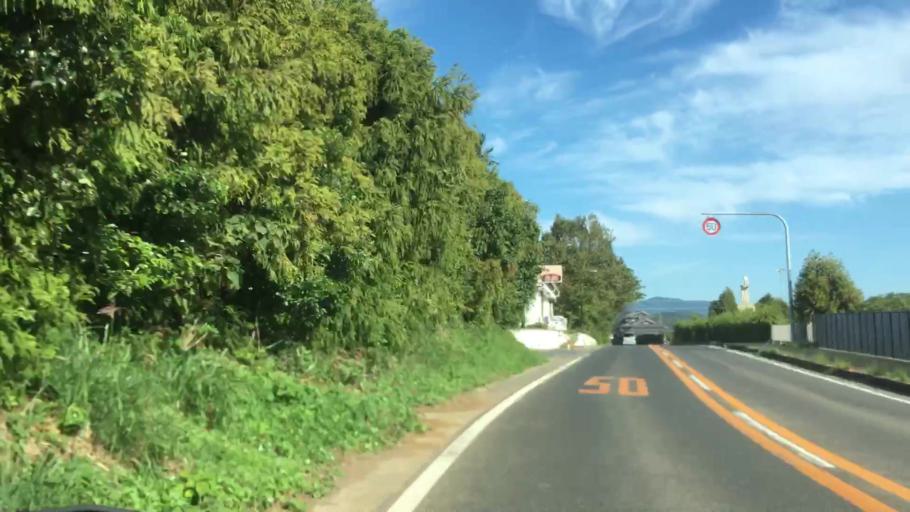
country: JP
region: Nagasaki
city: Sasebo
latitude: 33.0722
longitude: 129.7607
